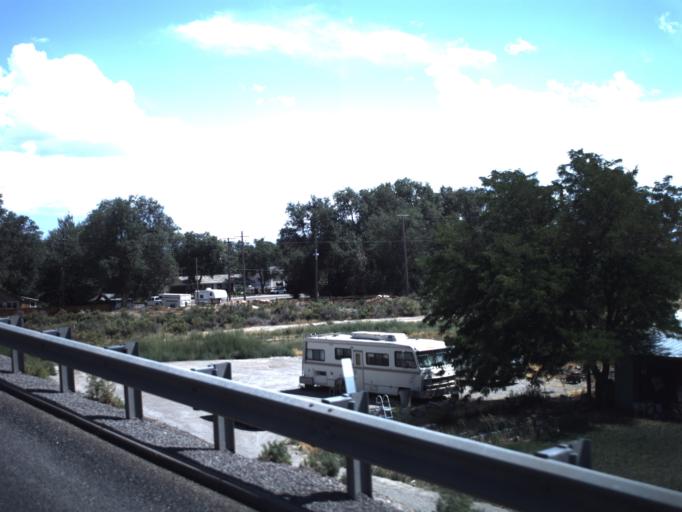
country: US
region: Utah
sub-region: Millard County
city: Delta
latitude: 39.3524
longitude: -112.5881
